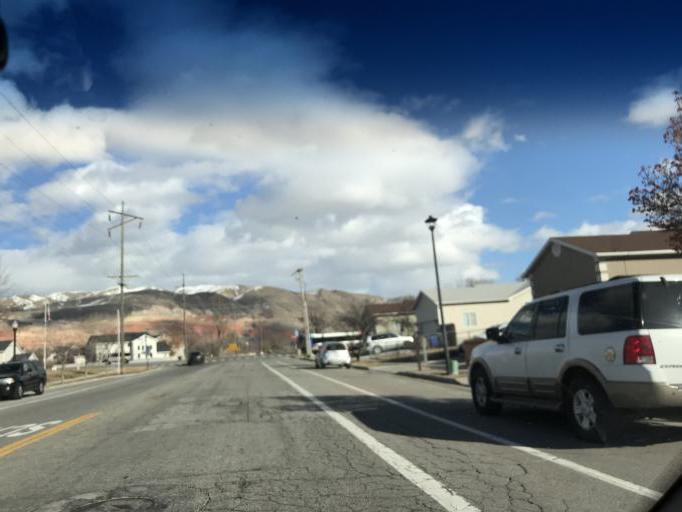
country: US
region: Utah
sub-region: Davis County
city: North Salt Lake
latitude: 40.8056
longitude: -111.9405
